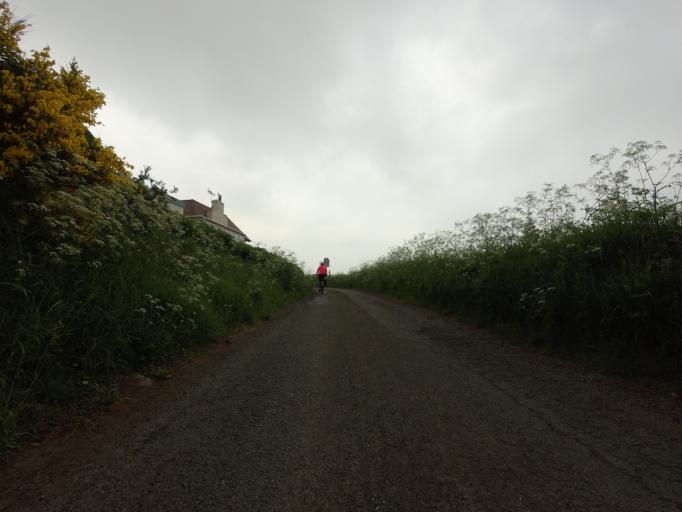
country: GB
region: Scotland
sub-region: Fife
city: Ballingry
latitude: 56.2294
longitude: -3.3426
